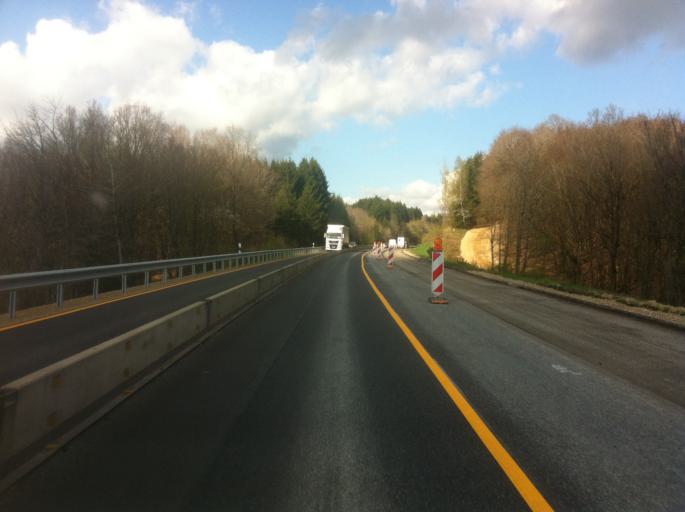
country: DE
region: Rheinland-Pfalz
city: Weinsheim
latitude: 50.2390
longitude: 6.4584
